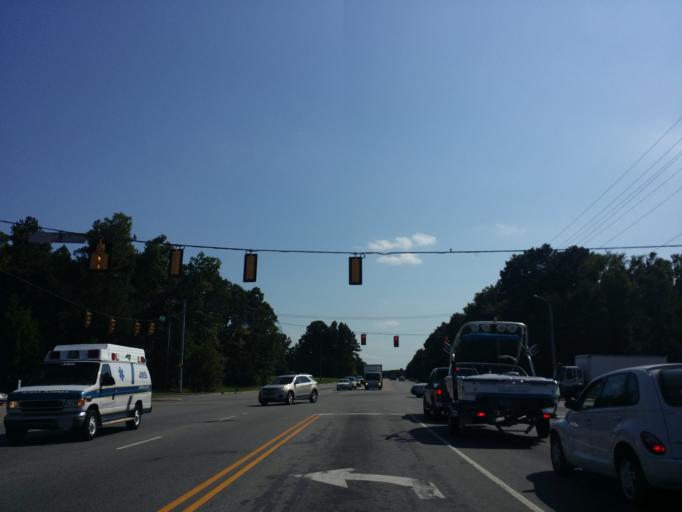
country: US
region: North Carolina
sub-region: Durham County
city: Durham
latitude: 35.9246
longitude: -78.8464
